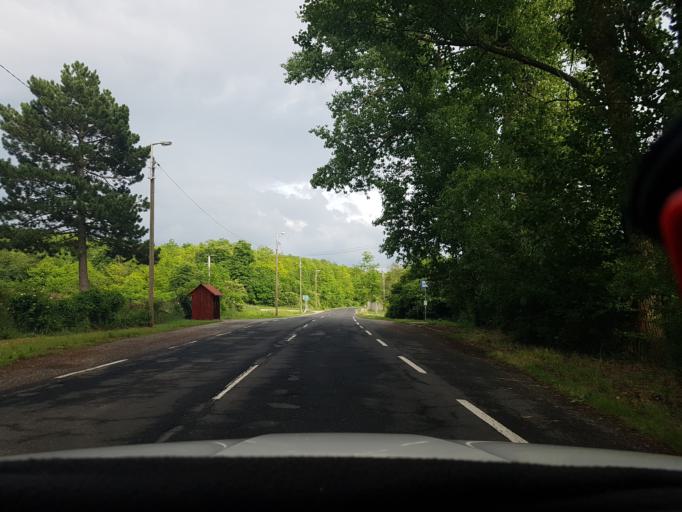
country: HU
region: Komarom-Esztergom
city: Tokod
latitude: 47.7014
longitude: 18.6542
